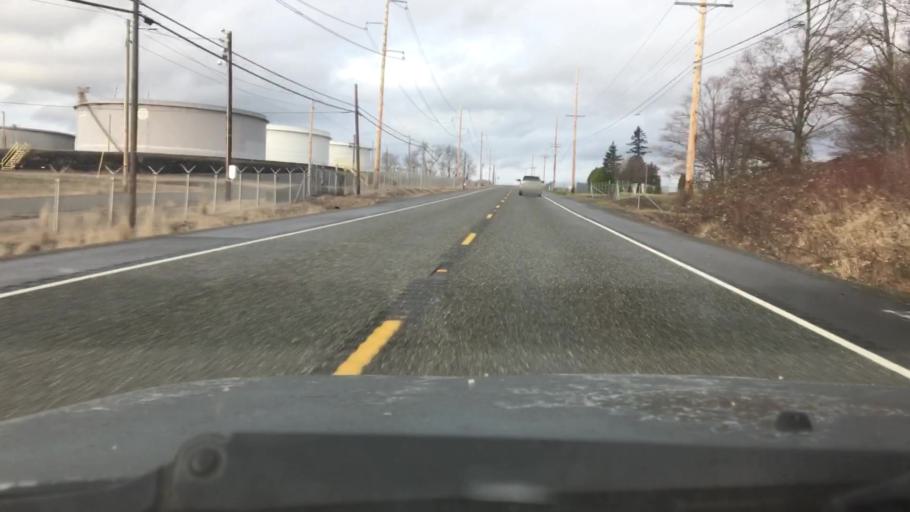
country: US
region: Washington
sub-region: Whatcom County
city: Ferndale
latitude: 48.8299
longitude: -122.6824
